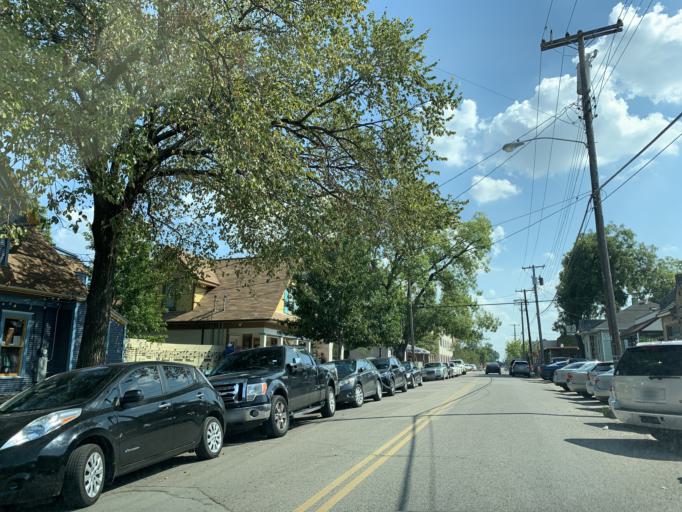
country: US
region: Texas
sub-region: Dallas County
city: Dallas
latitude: 32.7480
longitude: -96.8283
